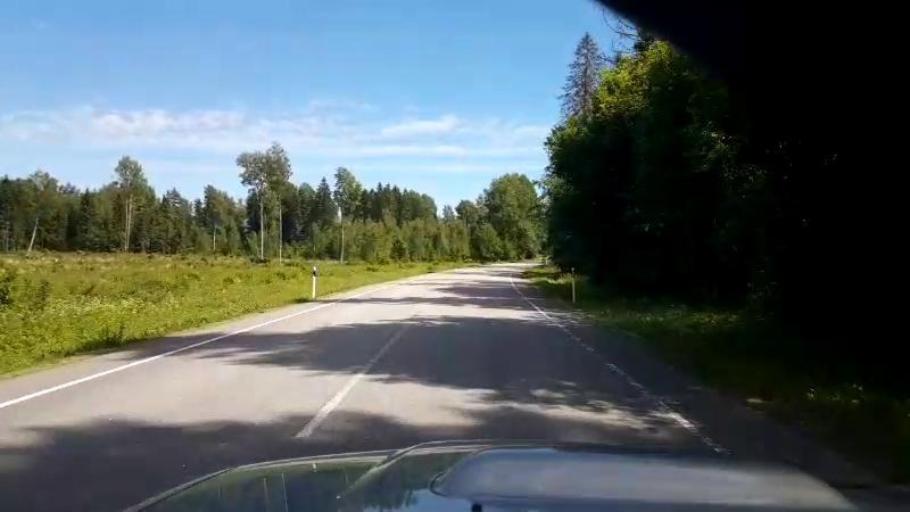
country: EE
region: Jaervamaa
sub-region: Koeru vald
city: Koeru
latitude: 58.9809
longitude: 26.0543
